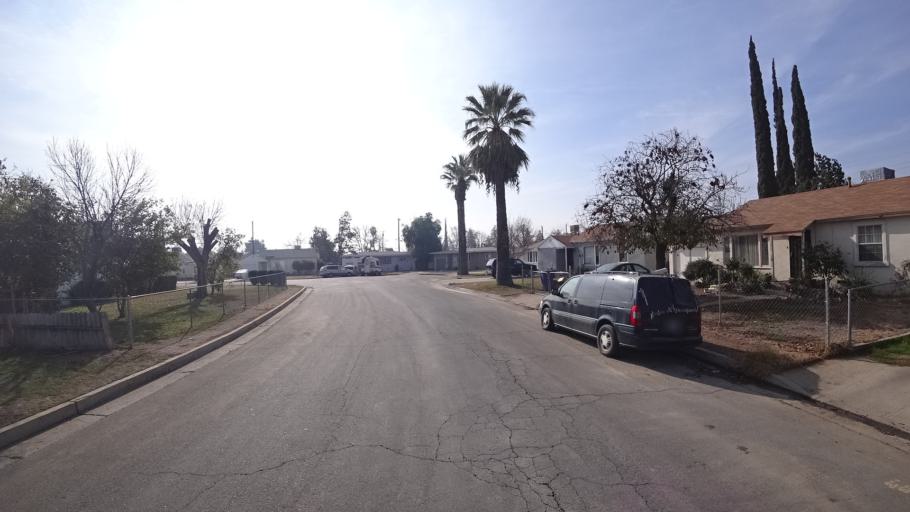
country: US
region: California
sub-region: Kern County
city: Bakersfield
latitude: 35.3492
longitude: -119.0180
